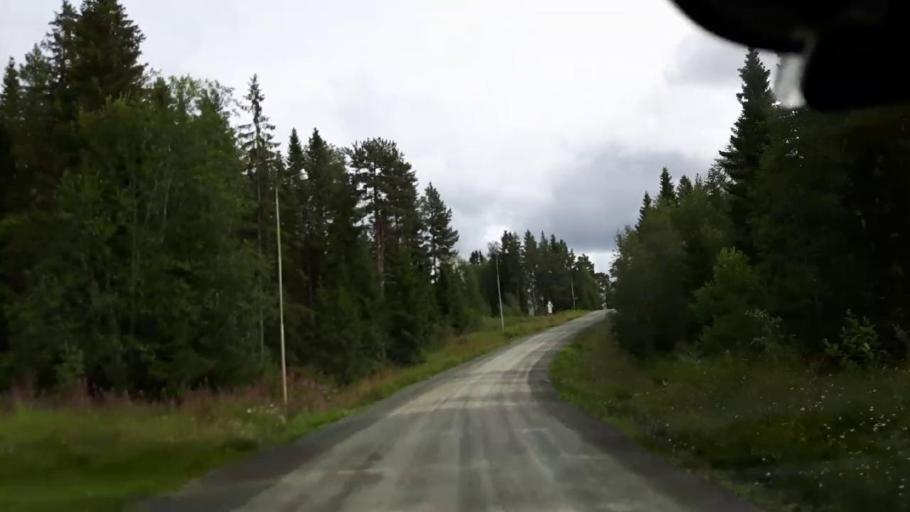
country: SE
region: Jaemtland
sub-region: Krokoms Kommun
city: Valla
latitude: 63.6259
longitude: 14.0386
